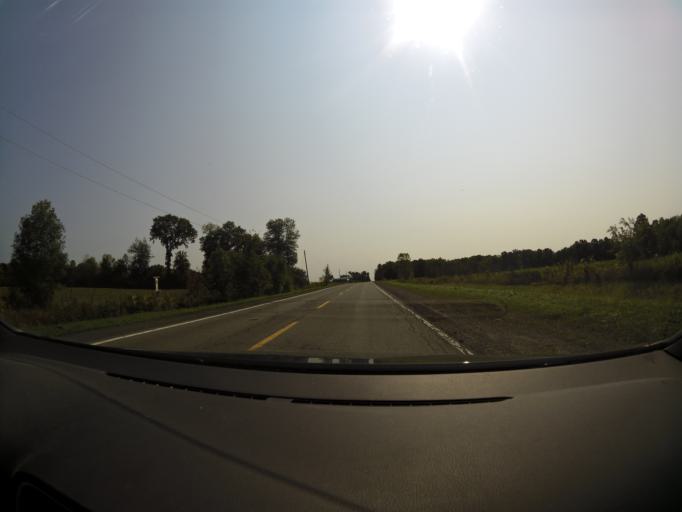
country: CA
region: Ontario
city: Arnprior
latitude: 45.4965
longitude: -76.2002
